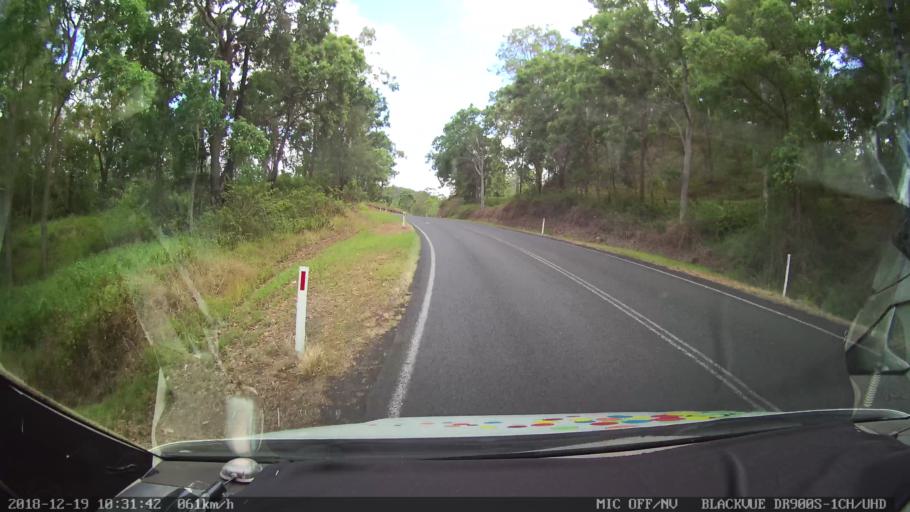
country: AU
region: New South Wales
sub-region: Lismore Municipality
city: Larnook
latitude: -28.5878
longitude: 153.1184
